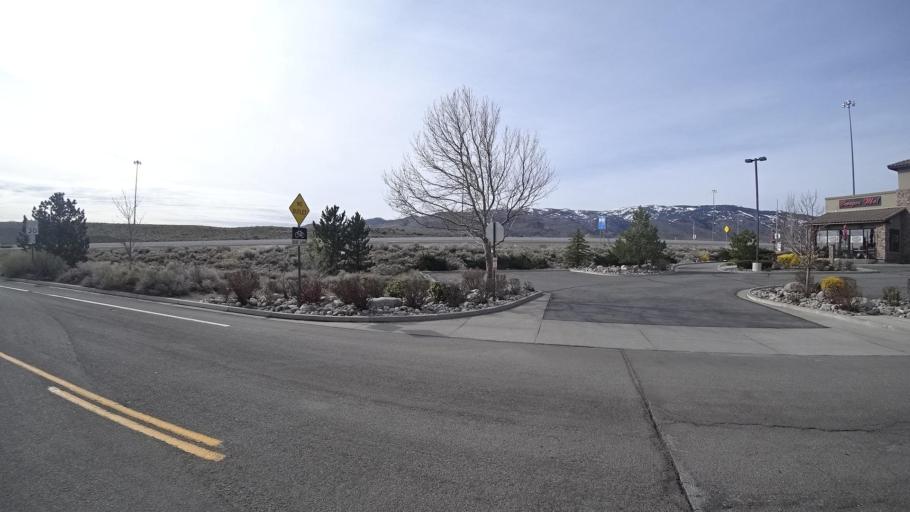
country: US
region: Nevada
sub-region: Washoe County
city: Mogul
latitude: 39.5173
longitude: -119.8854
